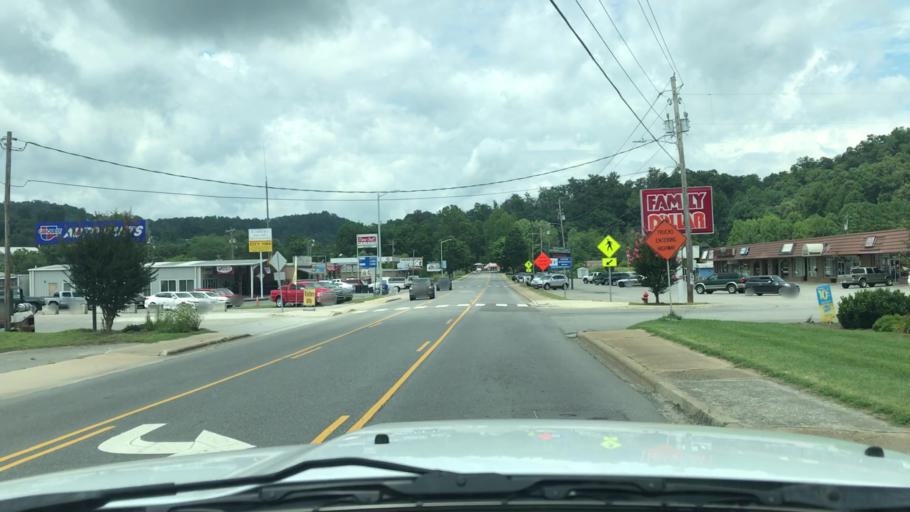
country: US
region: North Carolina
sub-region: Graham County
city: Robbinsville
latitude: 35.3259
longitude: -83.8036
